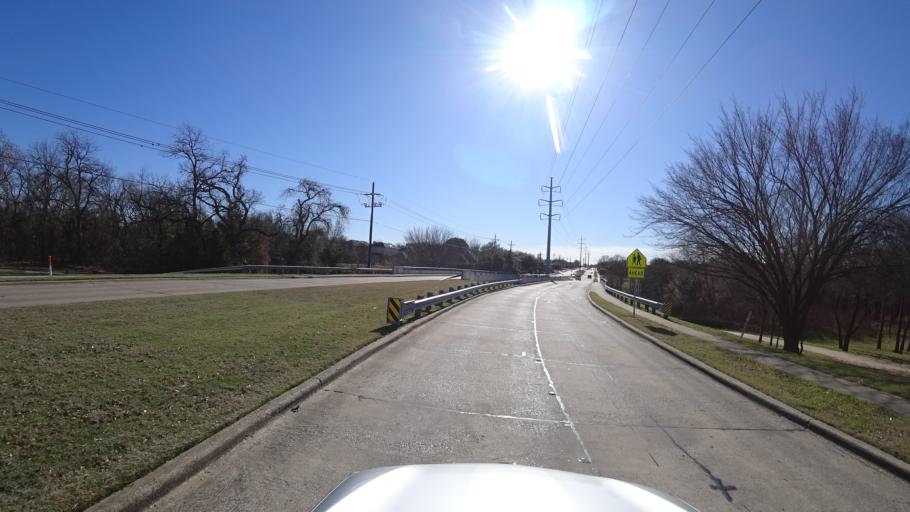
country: US
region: Texas
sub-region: Denton County
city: Lewisville
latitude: 33.0153
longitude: -97.0050
